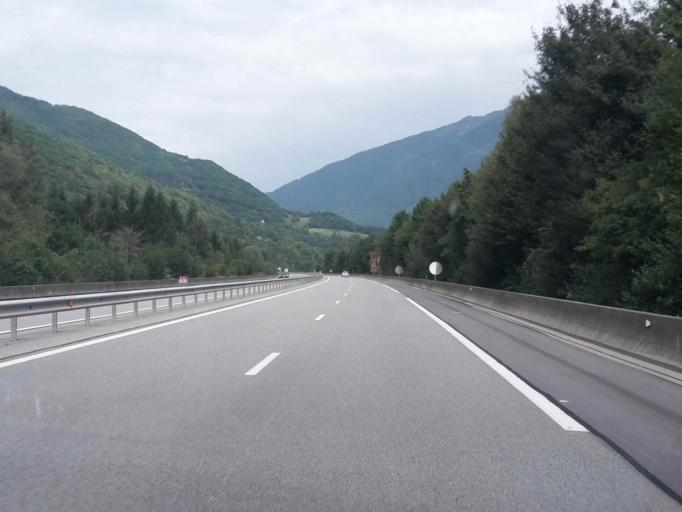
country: FR
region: Rhone-Alpes
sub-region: Departement de la Savoie
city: Aiton
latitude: 45.4907
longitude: 6.2958
